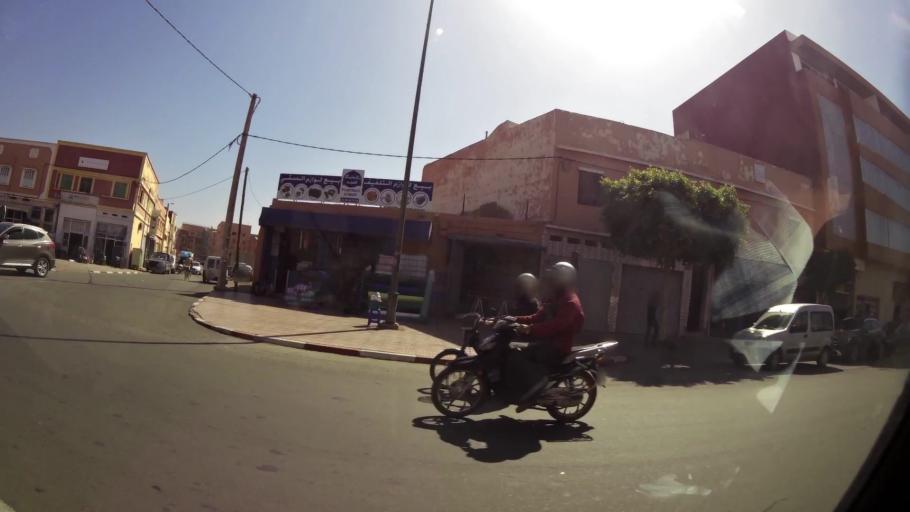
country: MA
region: Souss-Massa-Draa
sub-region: Inezgane-Ait Mellou
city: Inezgane
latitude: 30.3445
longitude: -9.5027
